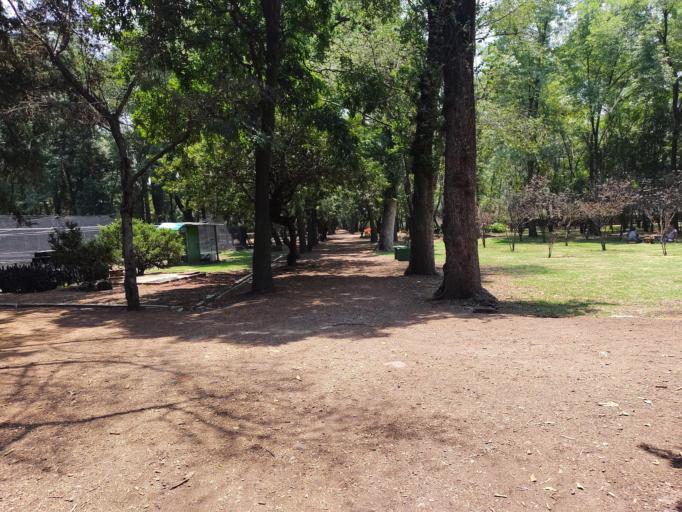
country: MX
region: Mexico City
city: Coyoacan
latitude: 19.3535
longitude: -99.1733
